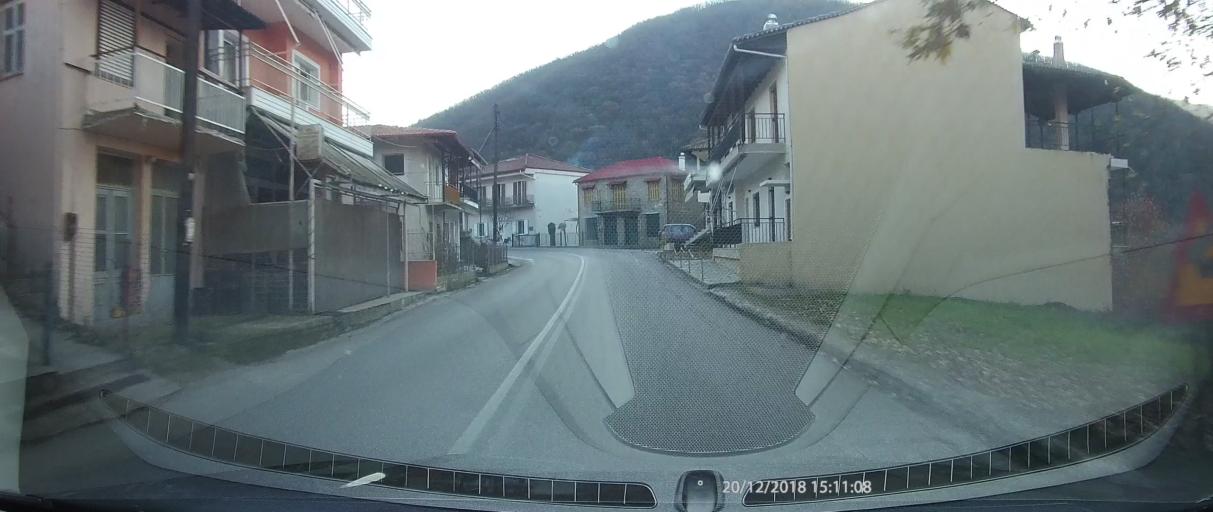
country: GR
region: Central Greece
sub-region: Nomos Fthiotidos
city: Makrakomi
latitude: 38.9470
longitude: 21.9560
